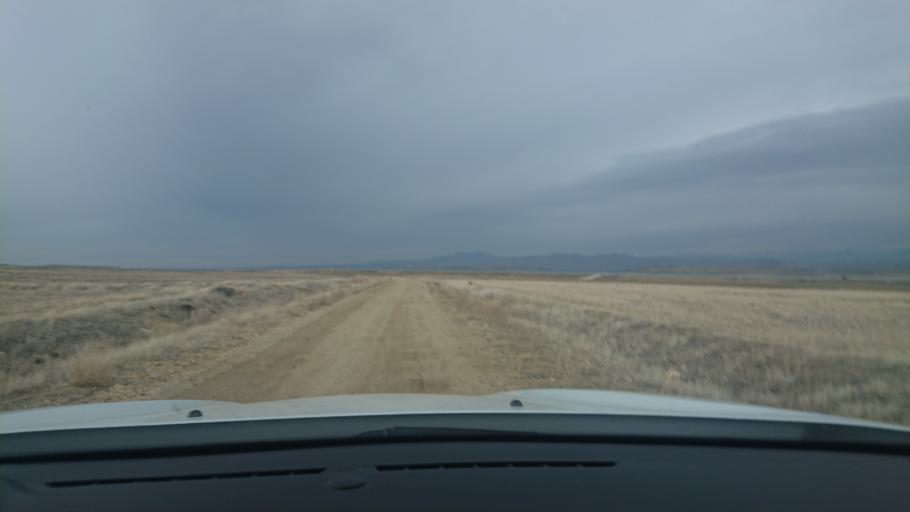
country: TR
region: Aksaray
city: Sariyahsi
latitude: 38.9821
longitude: 33.8777
